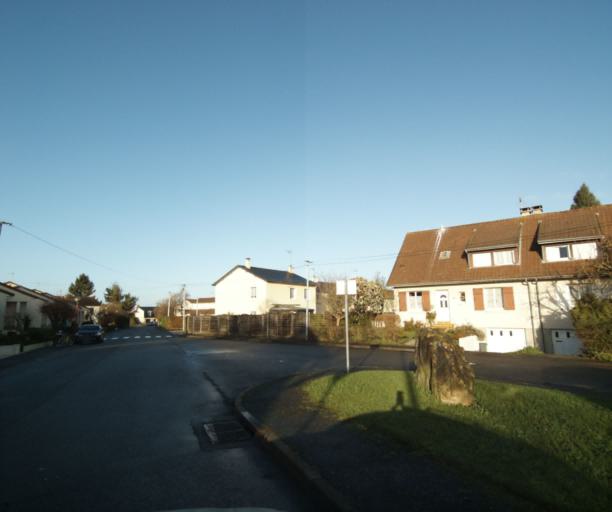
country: FR
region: Pays de la Loire
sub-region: Departement de la Sarthe
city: Sarge-les-le-Mans
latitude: 48.0177
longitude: 0.2289
